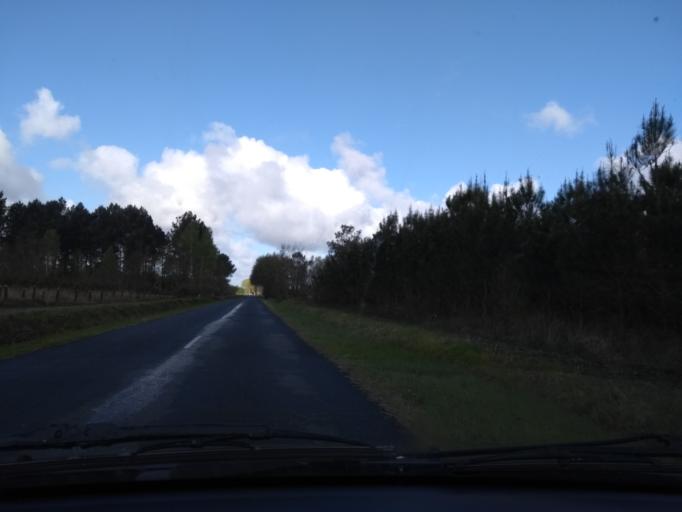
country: FR
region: Aquitaine
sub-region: Departement de la Gironde
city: Mios
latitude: 44.5500
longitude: -0.9779
